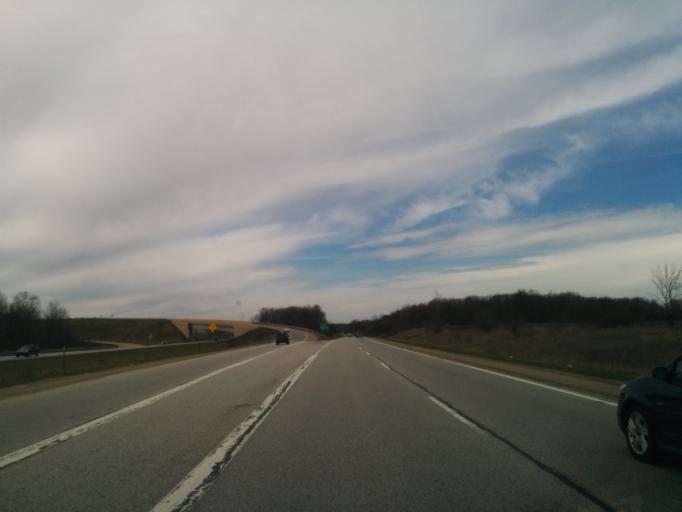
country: US
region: Michigan
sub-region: Ottawa County
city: Jenison
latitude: 42.8642
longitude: -85.8111
